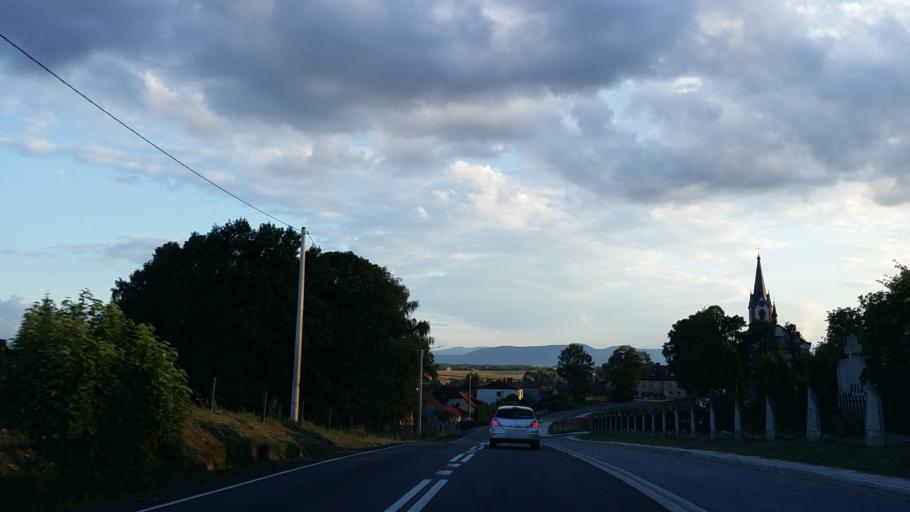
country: PL
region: Lesser Poland Voivodeship
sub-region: Powiat oswiecimski
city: Osiek
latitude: 49.9559
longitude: 19.2697
